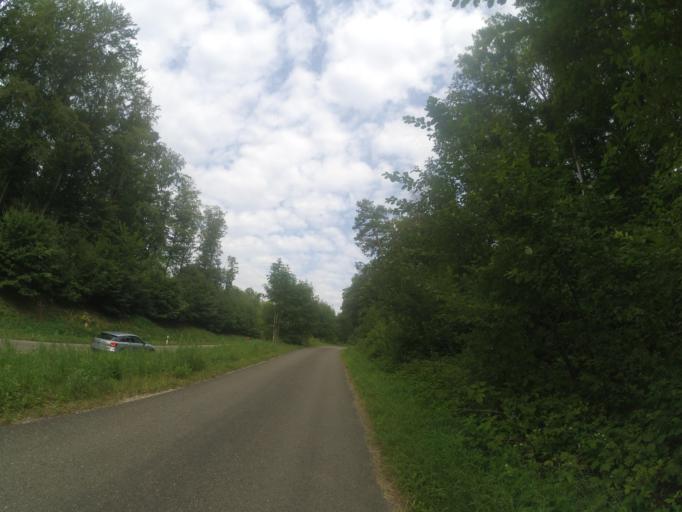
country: DE
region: Baden-Wuerttemberg
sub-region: Tuebingen Region
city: Lonsee
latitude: 48.5093
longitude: 9.9191
